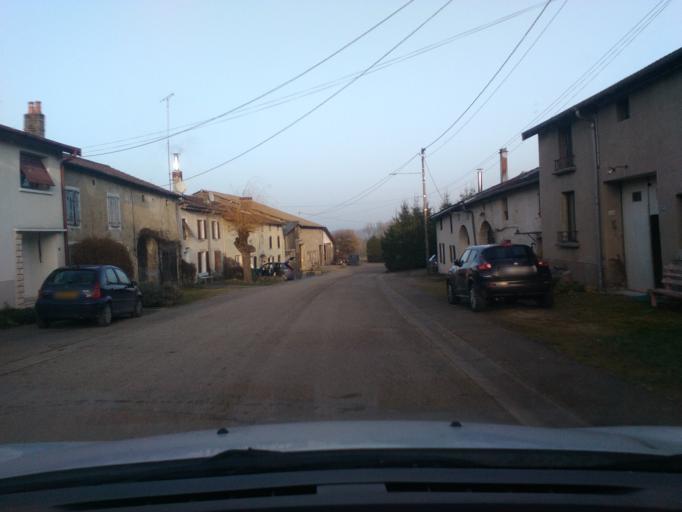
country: FR
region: Lorraine
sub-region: Departement des Vosges
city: Vittel
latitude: 48.2565
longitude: 6.0109
